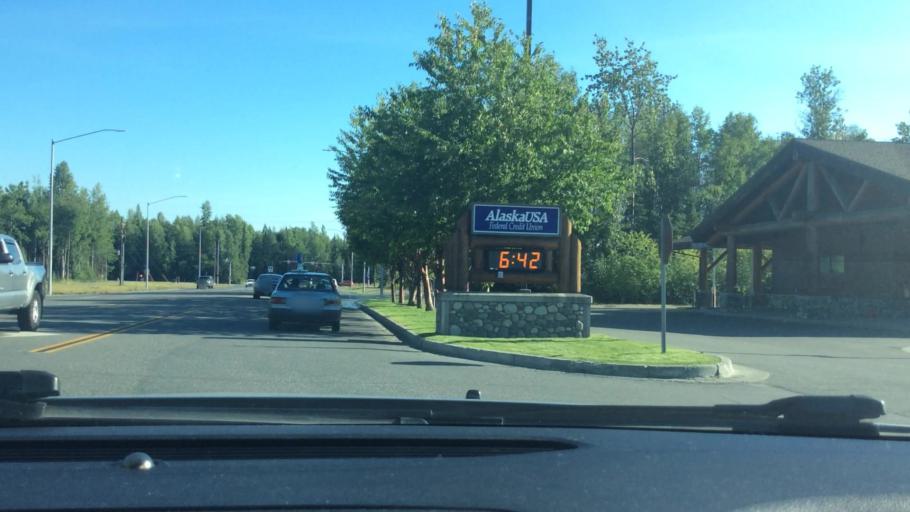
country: US
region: Alaska
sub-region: Anchorage Municipality
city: Elmendorf Air Force Base
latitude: 61.2337
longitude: -149.7619
